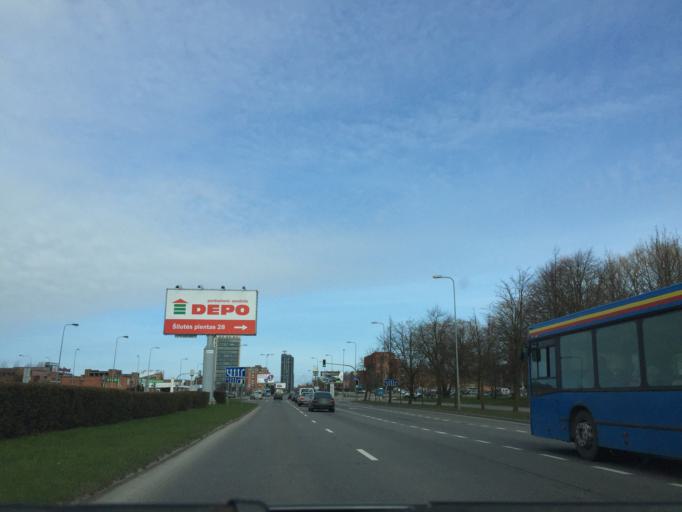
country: LT
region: Klaipedos apskritis
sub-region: Klaipeda
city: Klaipeda
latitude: 55.6885
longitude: 21.1568
